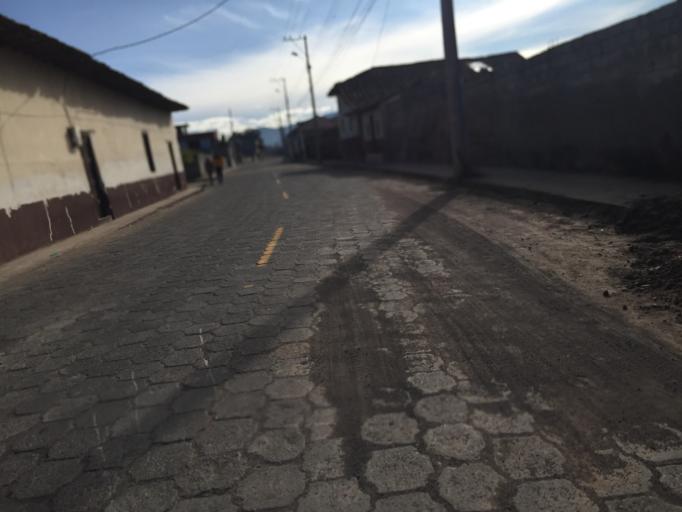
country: EC
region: Imbabura
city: Atuntaqui
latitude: 0.3374
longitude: -78.1975
